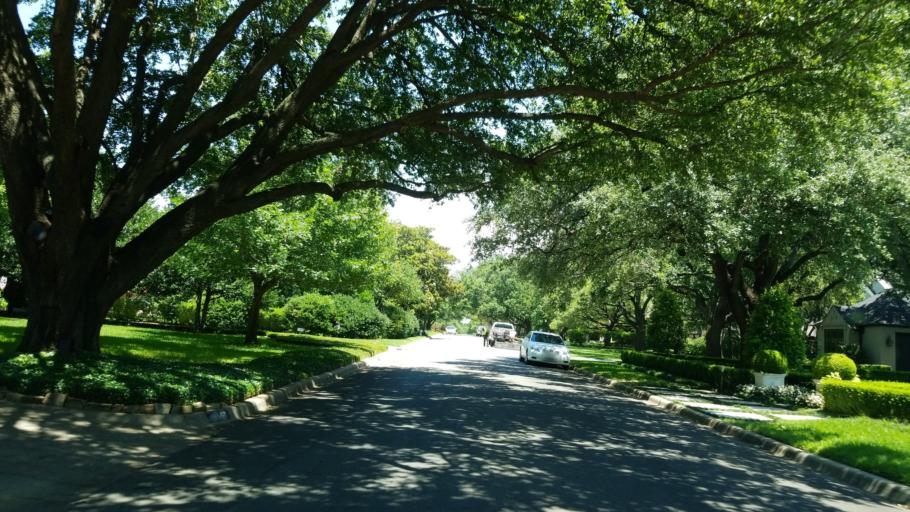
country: US
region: Texas
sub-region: Dallas County
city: University Park
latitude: 32.8726
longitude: -96.8368
